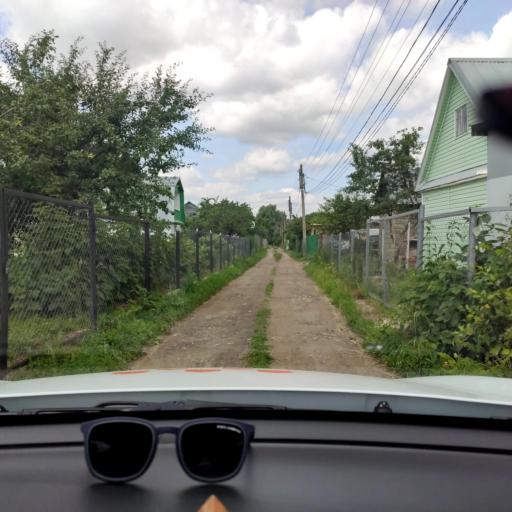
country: RU
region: Tatarstan
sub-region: Gorod Kazan'
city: Kazan
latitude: 55.8076
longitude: 49.2147
